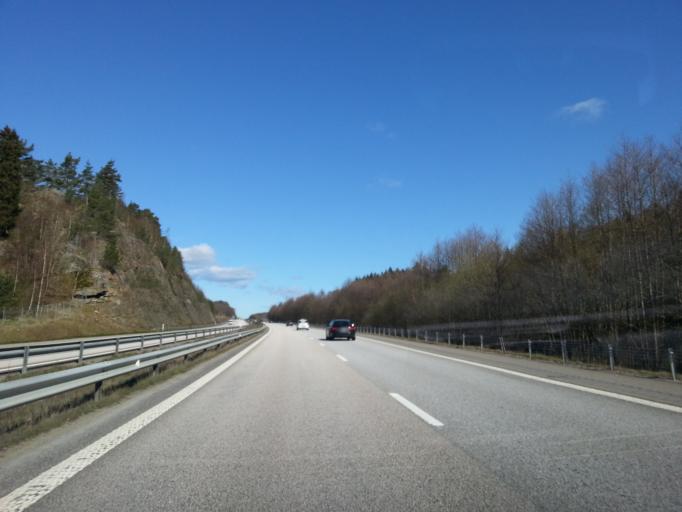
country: SE
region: Vaestra Goetaland
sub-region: Uddevalla Kommun
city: Ljungskile
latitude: 58.2436
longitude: 11.9092
